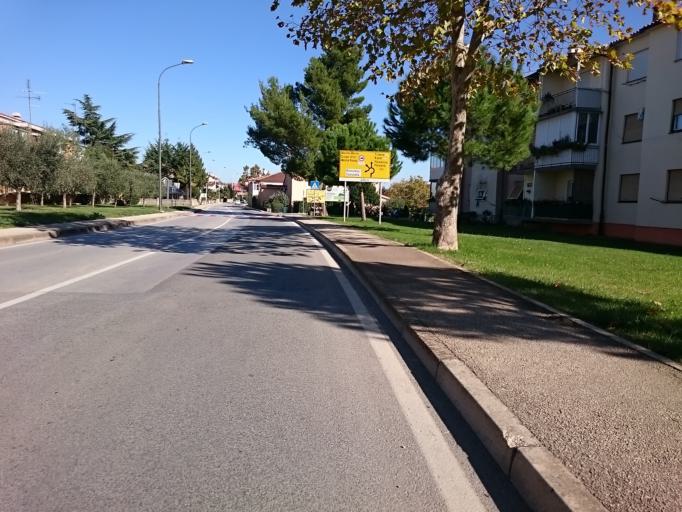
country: HR
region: Istarska
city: Umag
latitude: 45.4377
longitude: 13.5296
